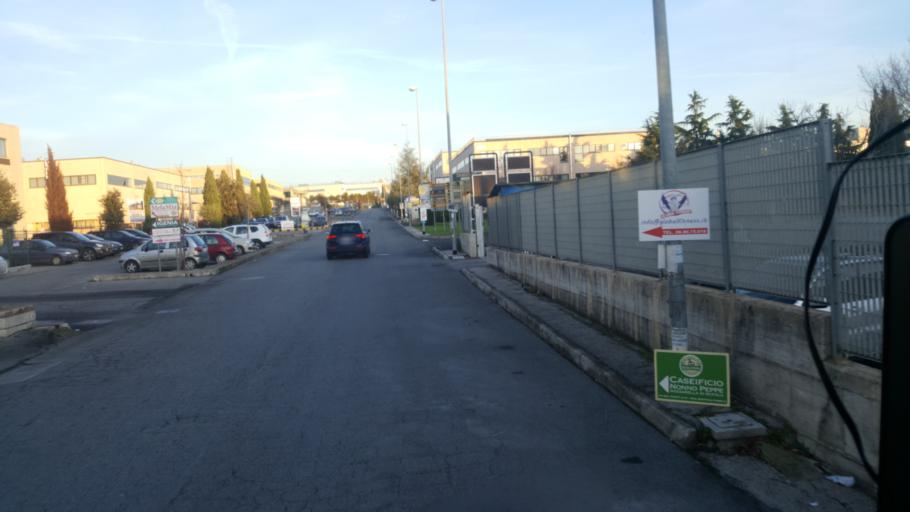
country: IT
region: Latium
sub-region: Citta metropolitana di Roma Capitale
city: Formello
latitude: 42.0500
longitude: 12.4007
